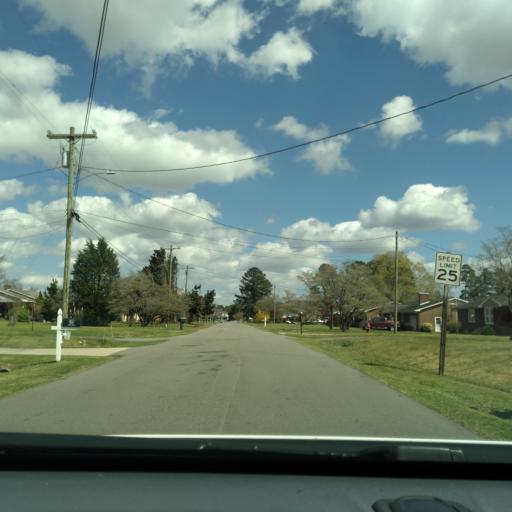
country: US
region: North Carolina
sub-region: Washington County
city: Plymouth
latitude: 35.8519
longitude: -76.7347
